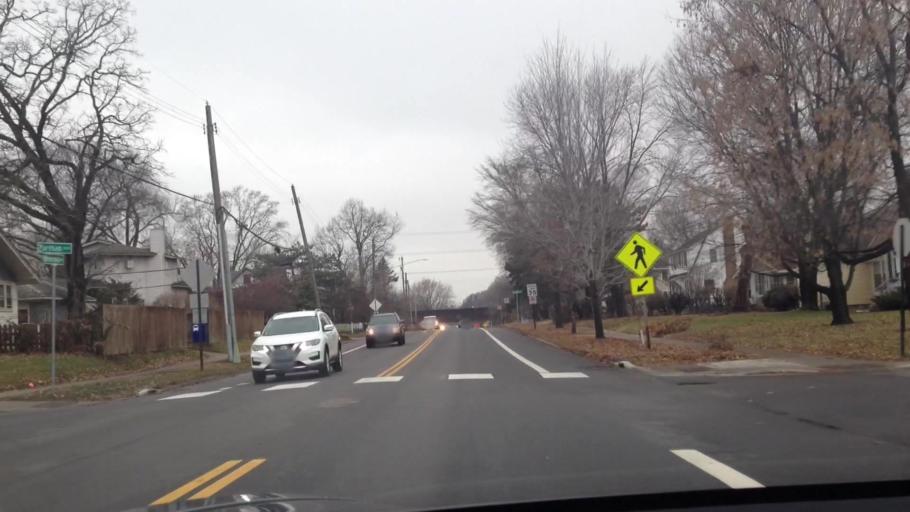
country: US
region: Minnesota
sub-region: Hennepin County
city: Saint Louis Park
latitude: 44.9494
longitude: -93.3543
